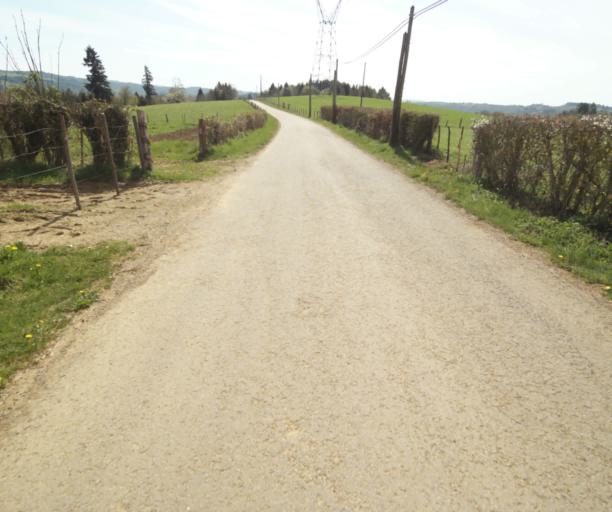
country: FR
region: Limousin
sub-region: Departement de la Correze
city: Naves
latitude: 45.3676
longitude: 1.8027
